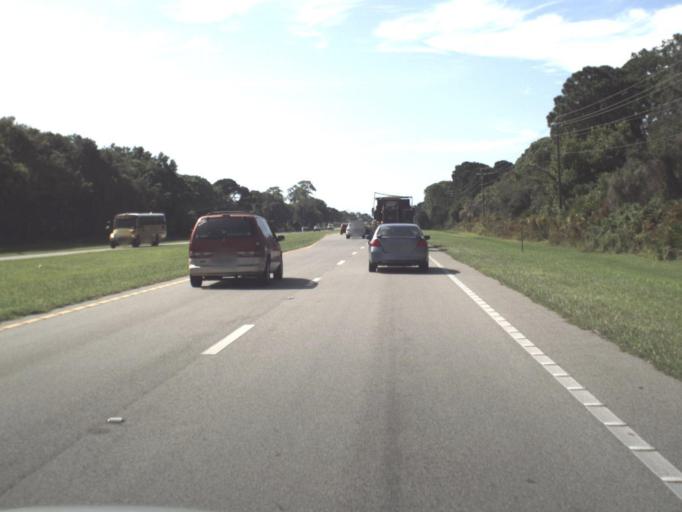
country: US
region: Florida
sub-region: Sarasota County
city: Vamo
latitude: 27.2132
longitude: -82.4904
